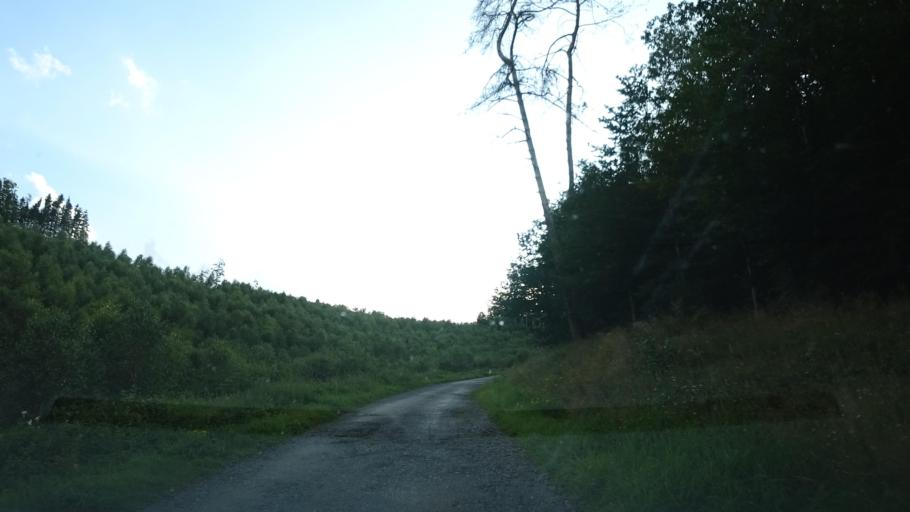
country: BE
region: Wallonia
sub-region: Province du Luxembourg
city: Herbeumont
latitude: 49.7827
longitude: 5.2514
